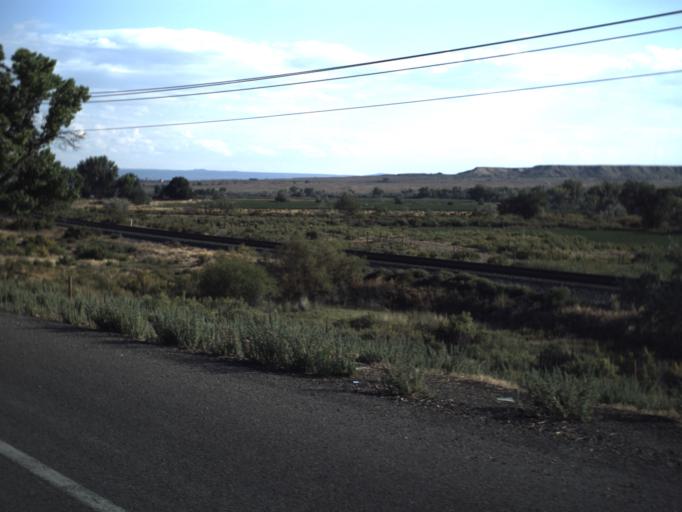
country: US
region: Utah
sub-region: Carbon County
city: Price
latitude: 39.5852
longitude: -110.7893
